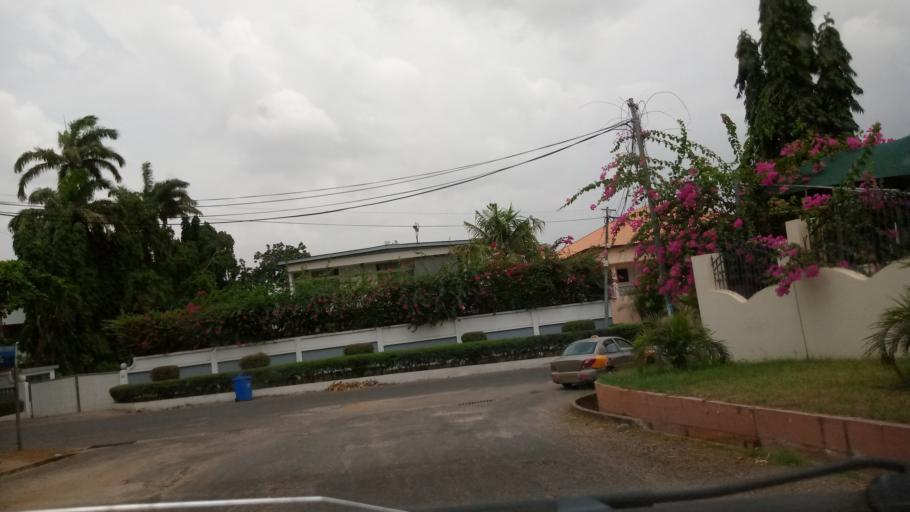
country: GH
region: Greater Accra
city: Accra
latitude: 5.6102
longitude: -0.1860
